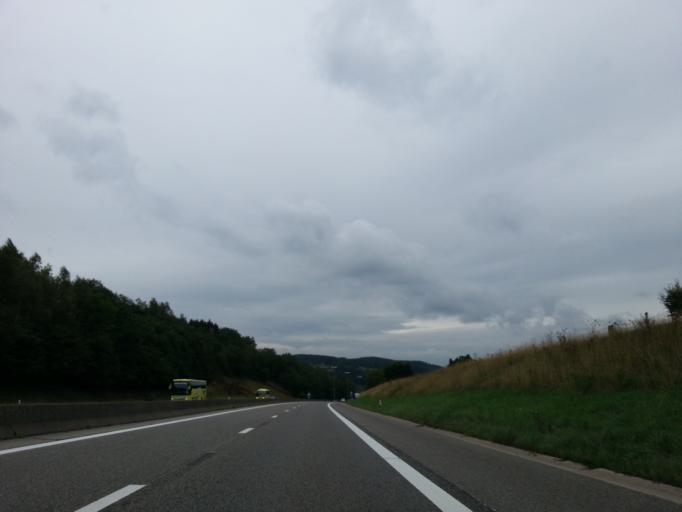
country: BE
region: Wallonia
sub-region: Province de Liege
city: Malmedy
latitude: 50.3620
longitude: 6.0375
